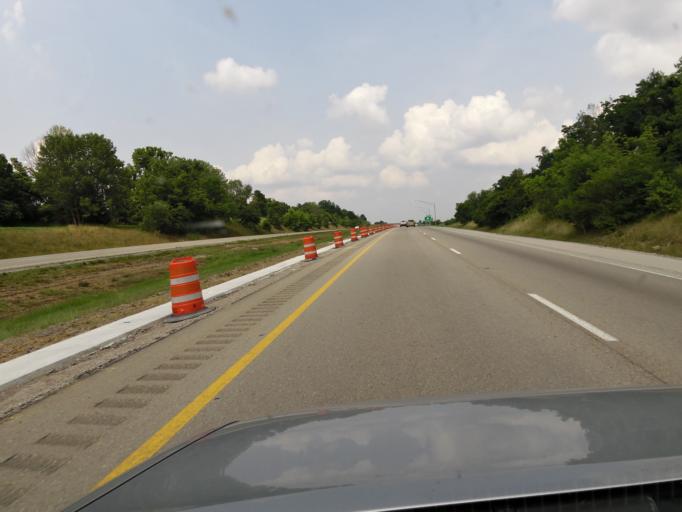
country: US
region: Kentucky
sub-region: Boone County
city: Verona
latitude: 38.8267
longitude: -84.6941
